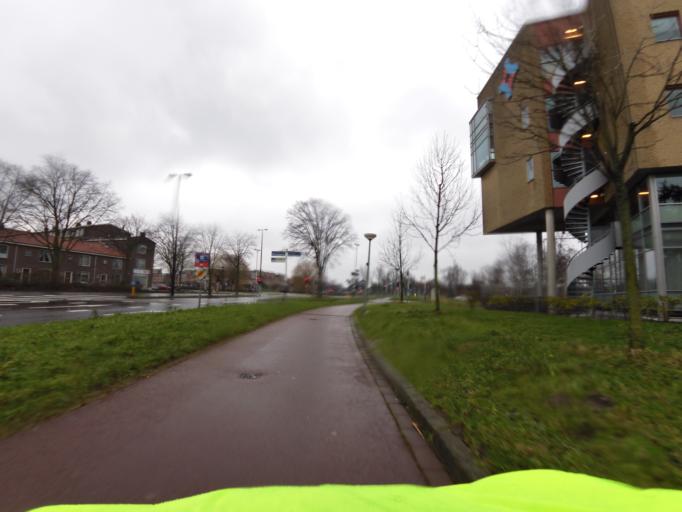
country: NL
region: South Holland
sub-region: Gemeente Vlaardingen
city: Vlaardingen
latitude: 51.9153
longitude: 4.3393
